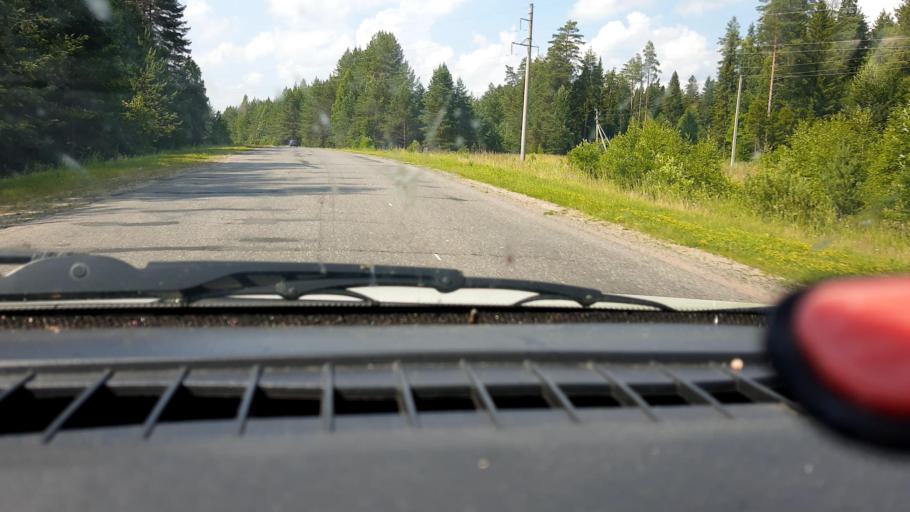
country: RU
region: Nizjnij Novgorod
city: Uren'
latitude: 57.4776
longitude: 46.0372
